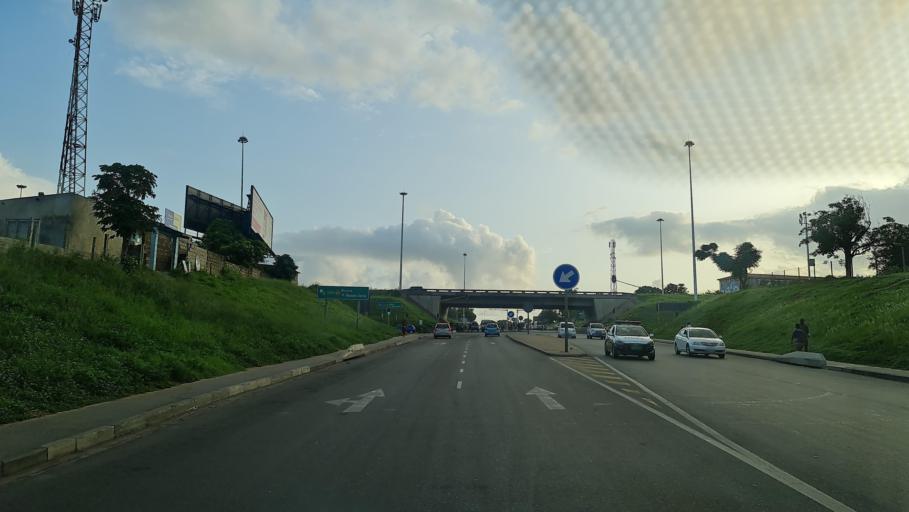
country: MZ
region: Maputo City
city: Maputo
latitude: -25.9447
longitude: 32.5400
